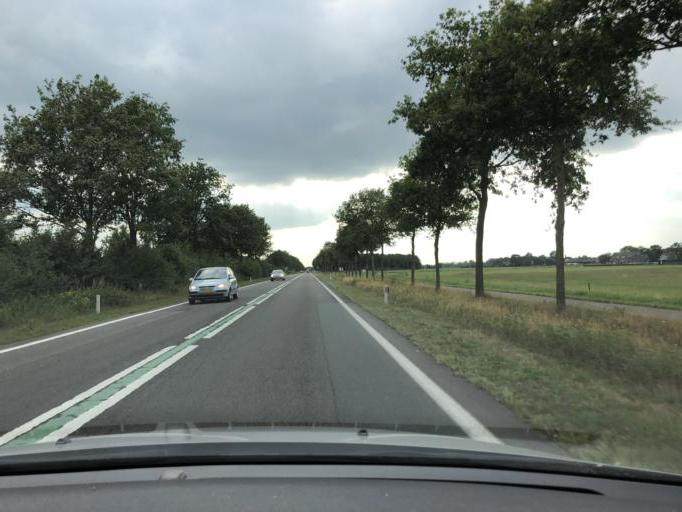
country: NL
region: Drenthe
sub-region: Gemeente Hoogeveen
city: Hoogeveen
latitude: 52.6131
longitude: 6.5066
